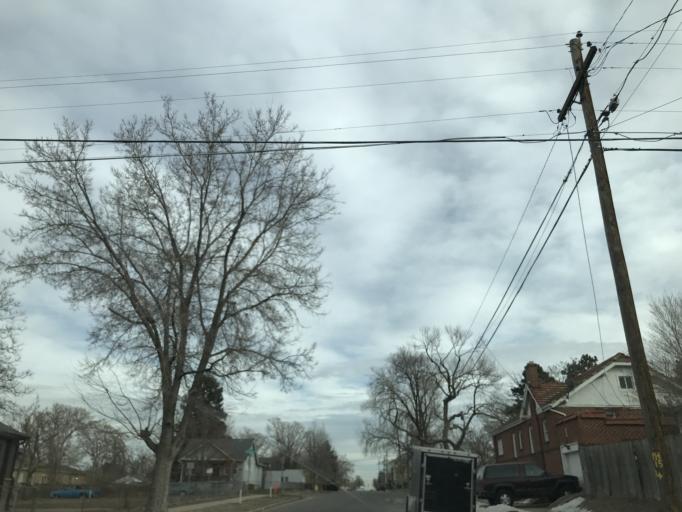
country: US
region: Colorado
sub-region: Adams County
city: Commerce City
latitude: 39.7789
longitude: -104.9560
